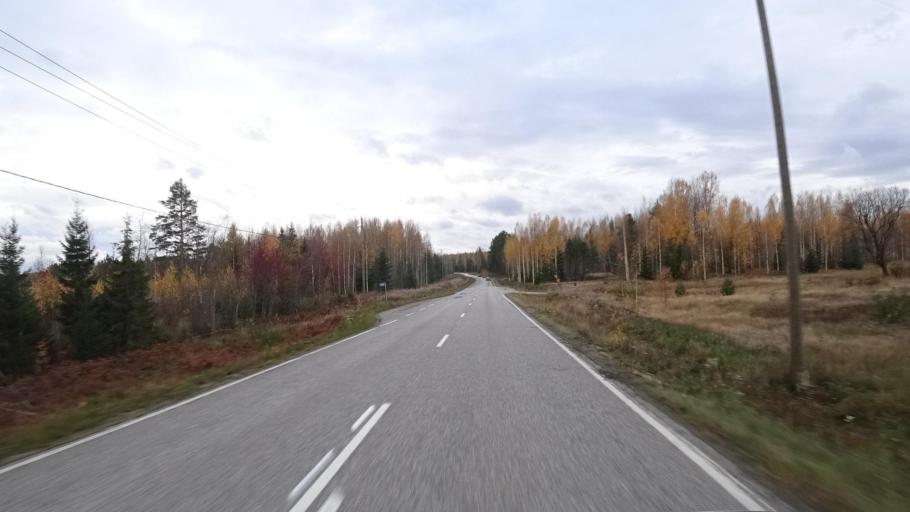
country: FI
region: Central Finland
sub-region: Joutsa
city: Joutsa
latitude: 61.8042
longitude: 26.1852
